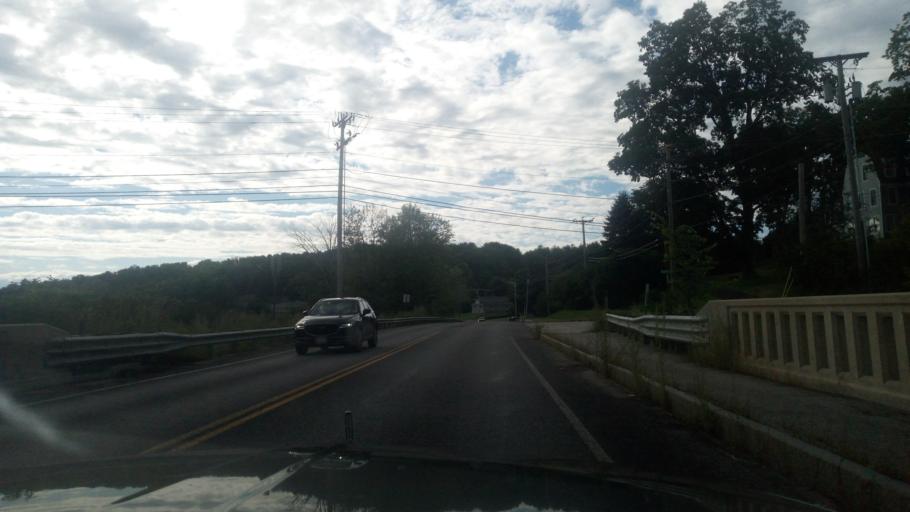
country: US
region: Maine
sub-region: Kennebec County
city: Gardiner
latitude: 44.2196
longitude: -69.7900
